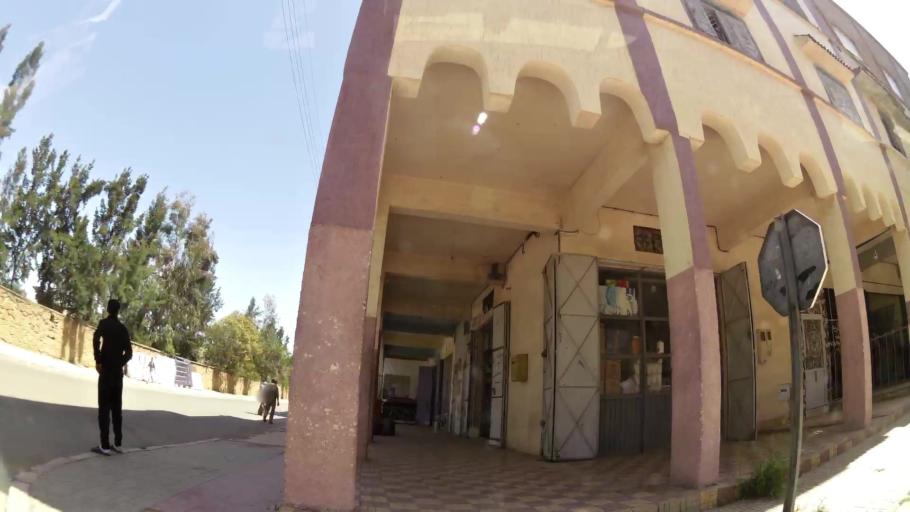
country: MA
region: Rabat-Sale-Zemmour-Zaer
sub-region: Khemisset
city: Khemisset
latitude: 33.8140
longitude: -6.0730
